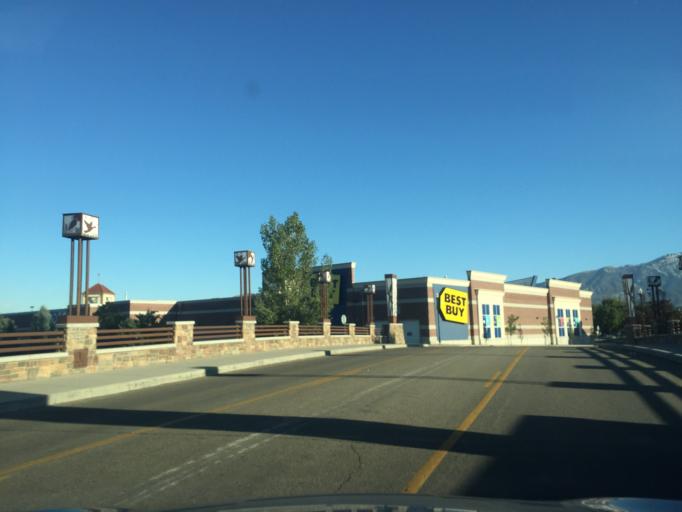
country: US
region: Utah
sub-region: Utah County
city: American Fork
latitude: 40.3833
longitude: -111.8194
